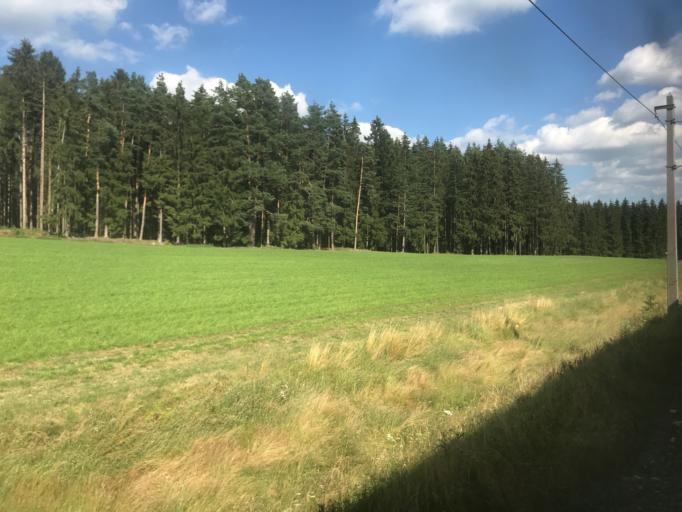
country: AT
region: Upper Austria
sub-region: Politischer Bezirk Urfahr-Umgebung
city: Reichenthal
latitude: 48.5741
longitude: 14.4492
